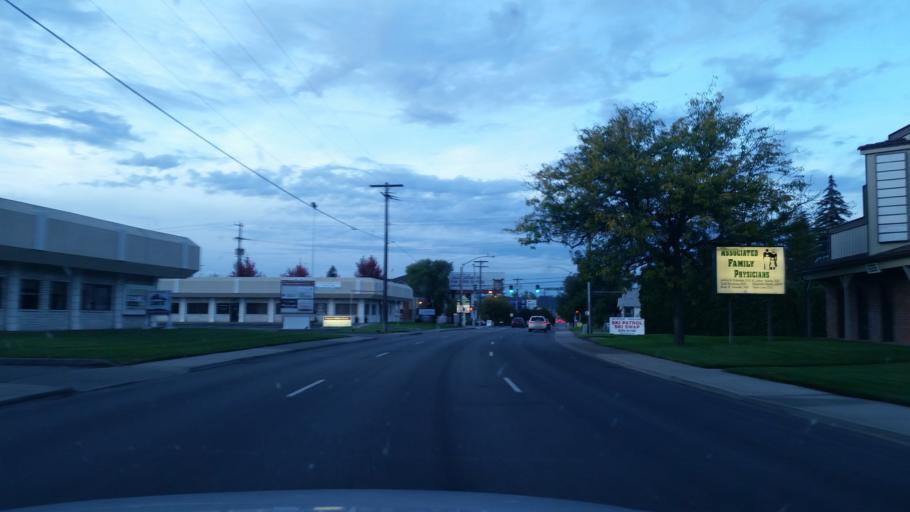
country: US
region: Washington
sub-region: Spokane County
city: Dishman
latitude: 47.6632
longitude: -117.2816
